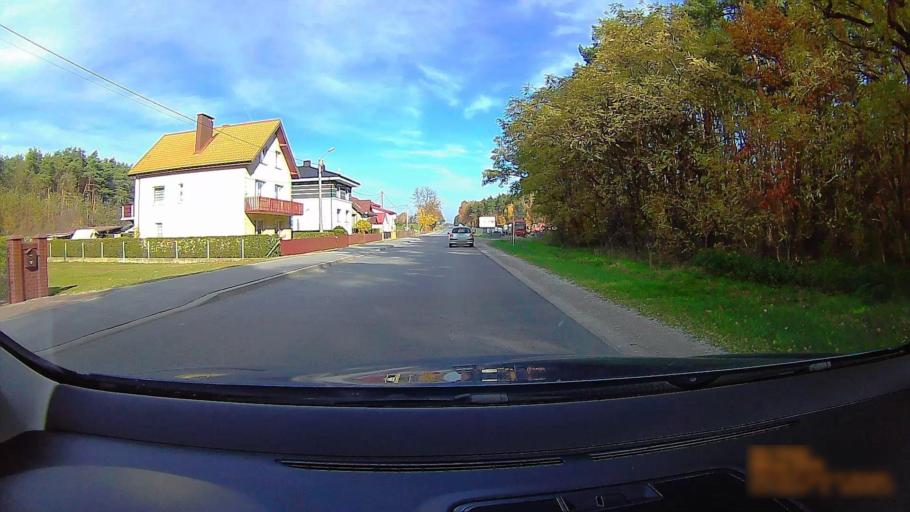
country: PL
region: Greater Poland Voivodeship
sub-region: Powiat ostrzeszowski
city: Doruchow
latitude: 51.3687
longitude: 18.0327
